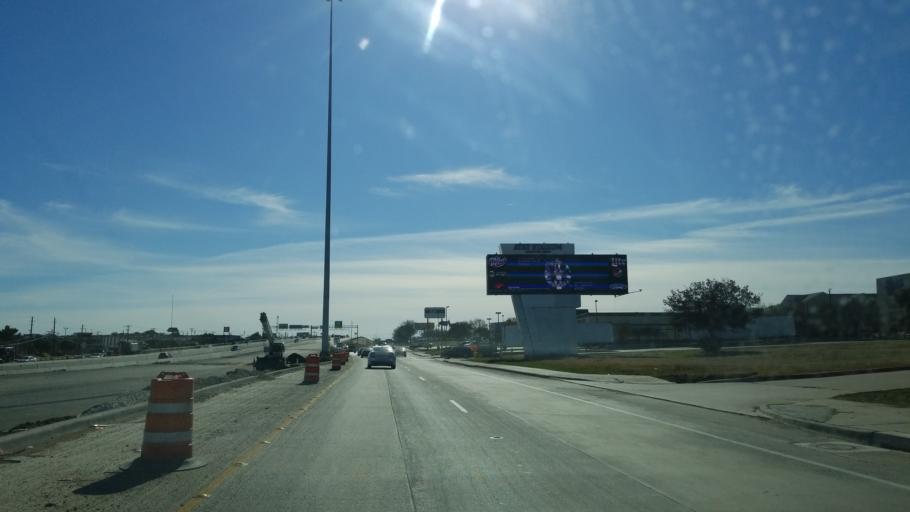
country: US
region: Texas
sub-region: Tarrant County
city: Arlington
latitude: 32.7553
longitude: -97.0638
